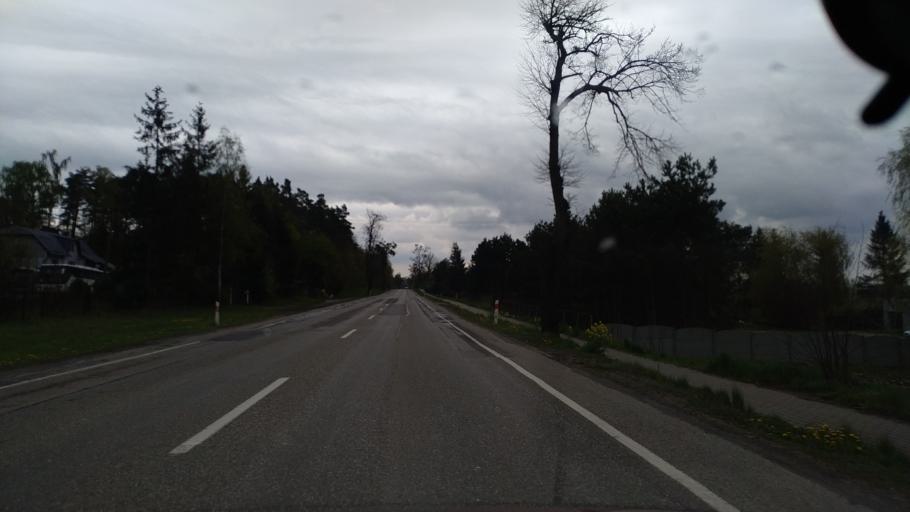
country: PL
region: Pomeranian Voivodeship
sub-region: Powiat tczewski
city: Pelplin
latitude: 54.0290
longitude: 18.6467
